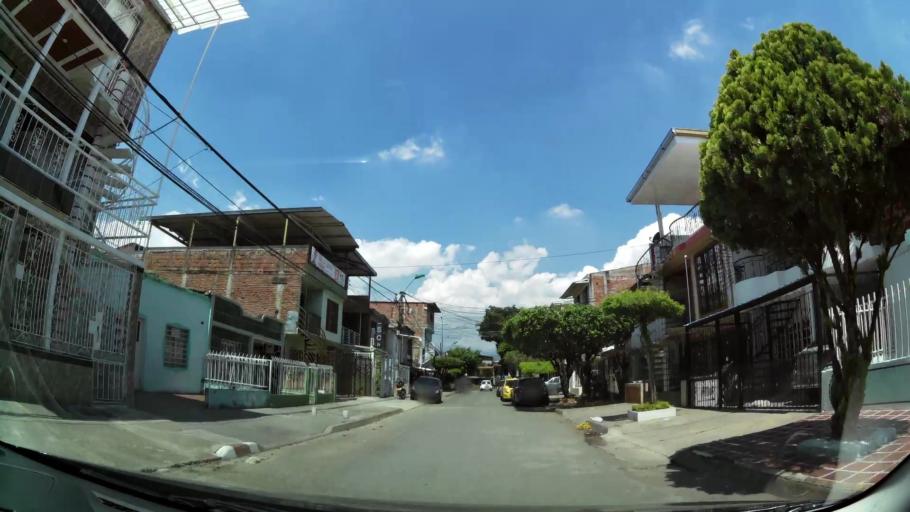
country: CO
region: Valle del Cauca
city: Cali
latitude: 3.4323
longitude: -76.5012
